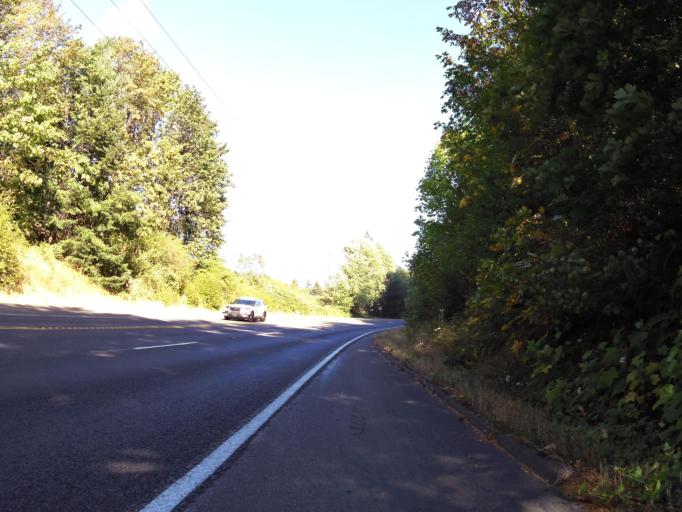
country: US
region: Washington
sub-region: Thurston County
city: Olympia
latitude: 47.0452
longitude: -122.9789
